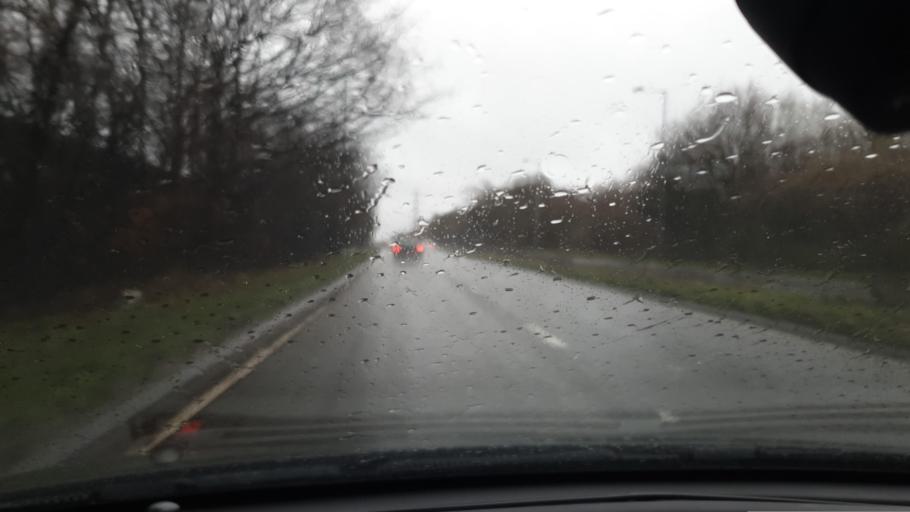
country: GB
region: England
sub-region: Walsall
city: Willenhall
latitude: 52.5806
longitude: -2.0635
